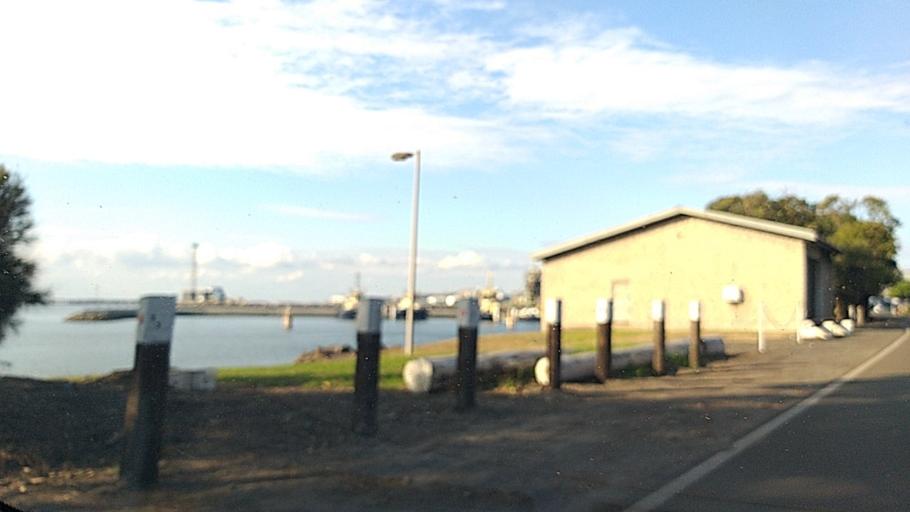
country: AU
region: New South Wales
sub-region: Wollongong
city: Port Kembla
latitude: -34.4658
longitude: 150.8998
